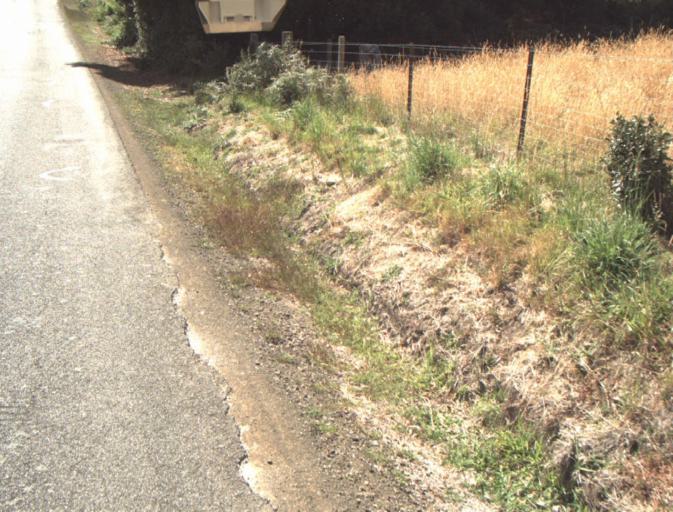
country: AU
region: Tasmania
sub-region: Launceston
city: Mayfield
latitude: -41.2587
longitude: 147.1864
